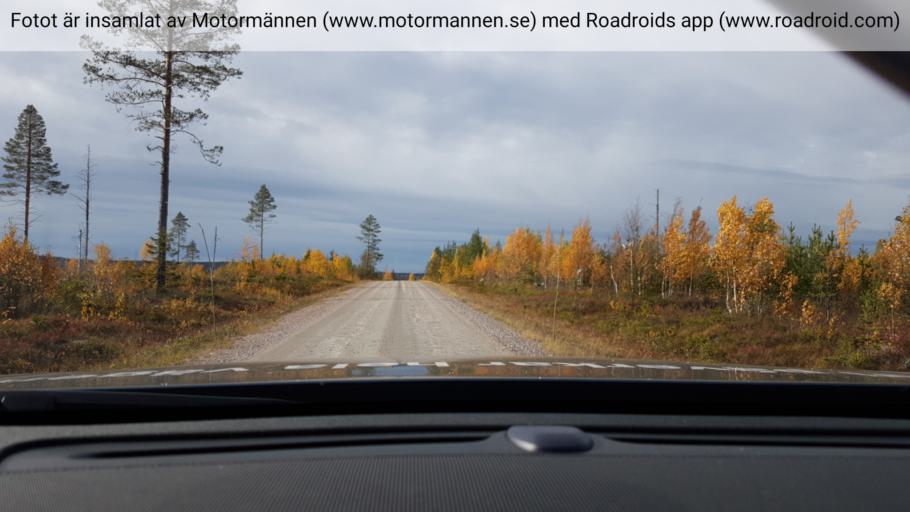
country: SE
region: Norrbotten
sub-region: Overkalix Kommun
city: OEverkalix
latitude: 66.2504
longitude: 23.1926
